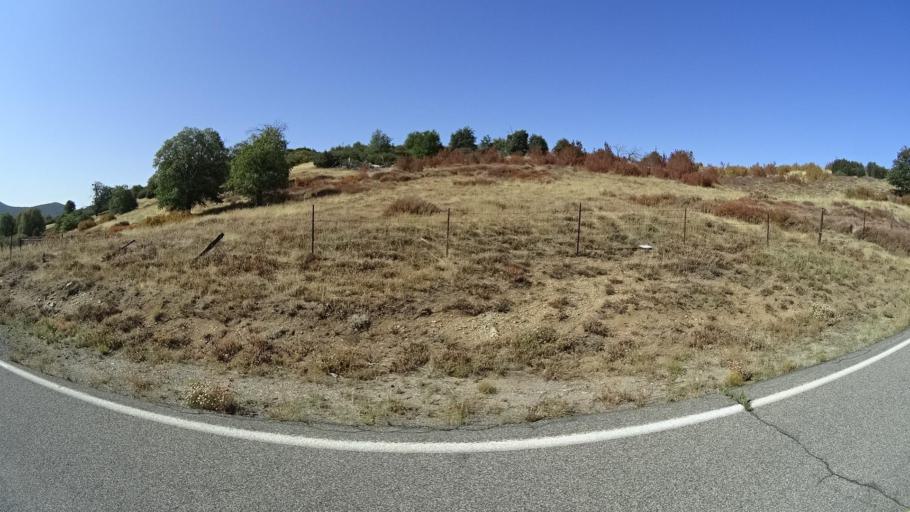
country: US
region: California
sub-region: San Diego County
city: Pine Valley
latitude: 32.9439
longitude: -116.4929
